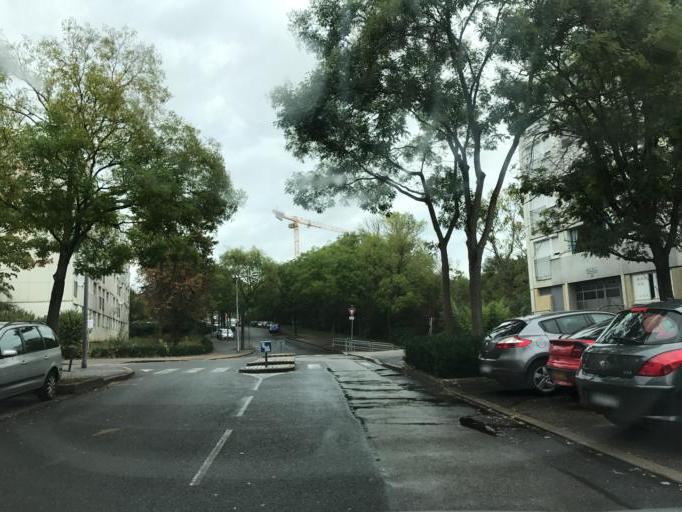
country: FR
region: Rhone-Alpes
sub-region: Departement du Rhone
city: Rillieux-la-Pape
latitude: 45.8127
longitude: 4.9050
